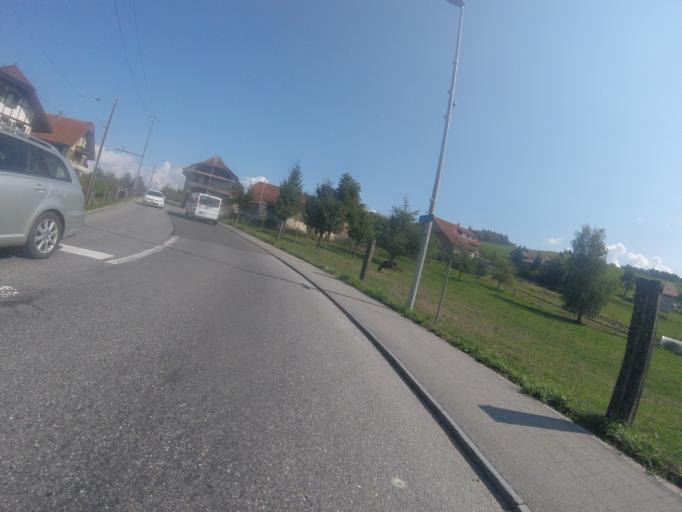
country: CH
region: Bern
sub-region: Thun District
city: Seftigen
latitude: 46.7867
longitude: 7.5420
